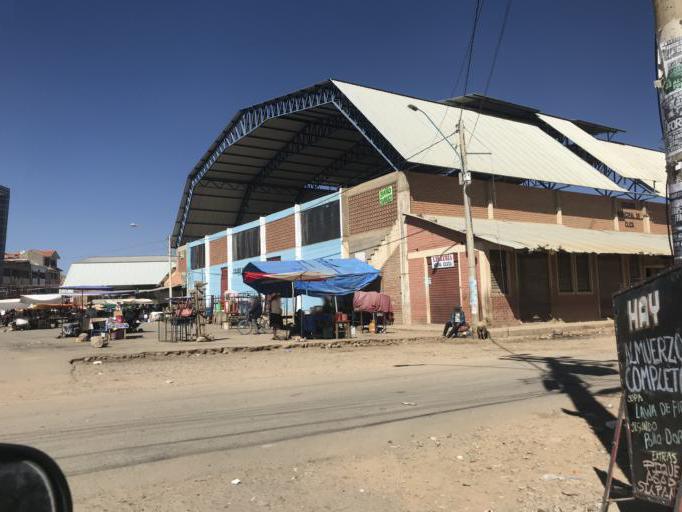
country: BO
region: Cochabamba
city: Cliza
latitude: -17.5933
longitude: -65.9361
